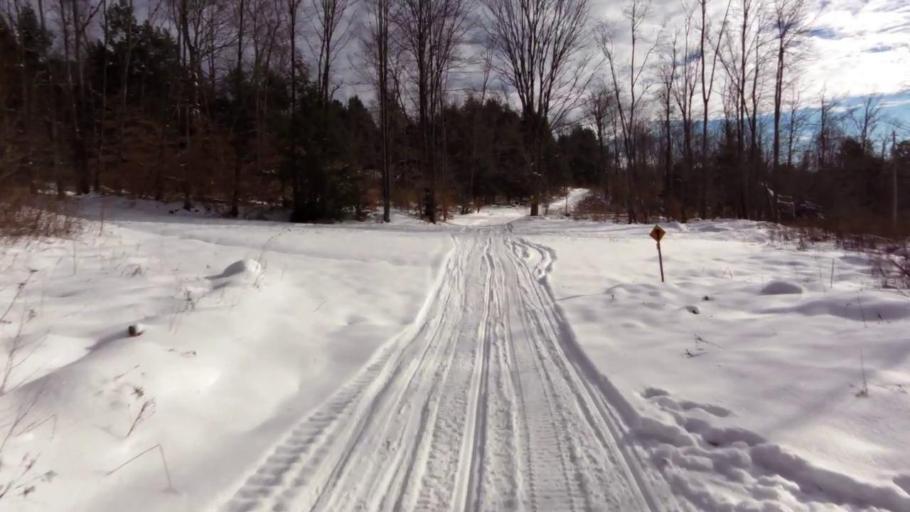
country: US
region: Pennsylvania
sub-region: McKean County
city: Foster Brook
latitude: 42.0051
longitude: -78.5421
